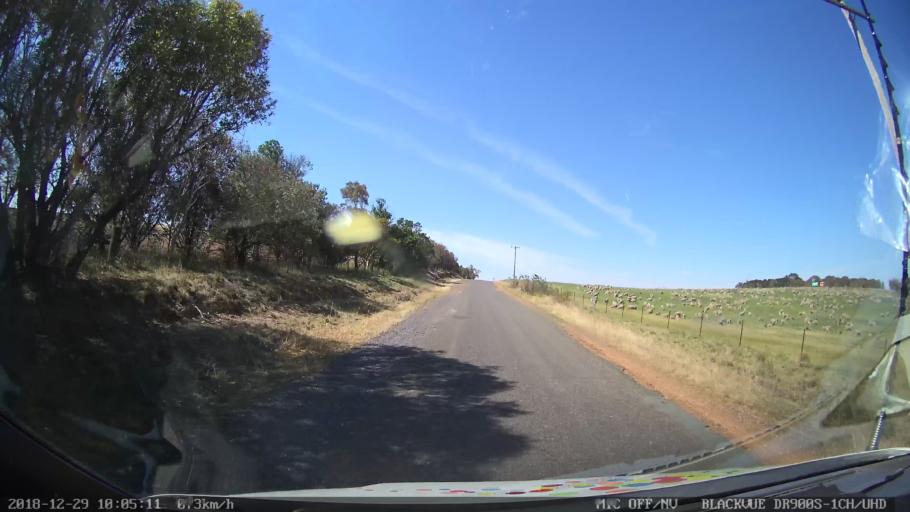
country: AU
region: New South Wales
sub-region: Goulburn Mulwaree
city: Goulburn
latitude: -34.8305
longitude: 149.4537
